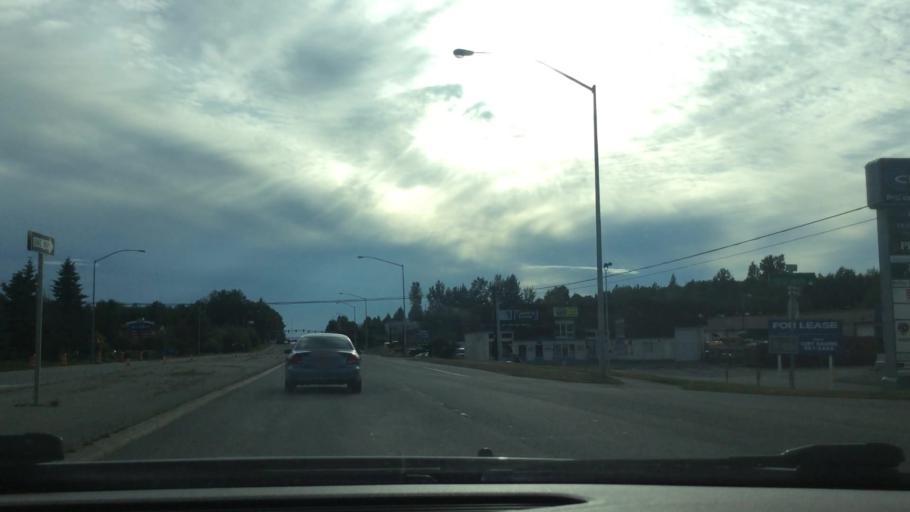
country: US
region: Alaska
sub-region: Anchorage Municipality
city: Anchorage
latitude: 61.1809
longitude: -149.8889
